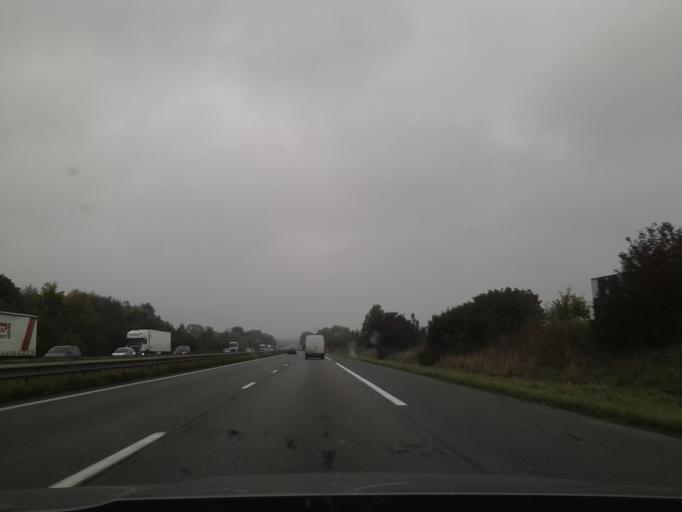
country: FR
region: Nord-Pas-de-Calais
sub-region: Departement du Nord
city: Prouvy
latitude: 50.3325
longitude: 3.4438
